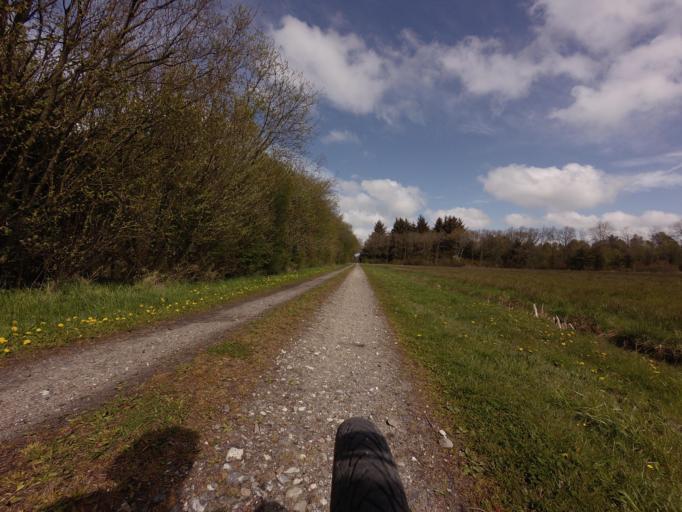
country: DK
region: North Denmark
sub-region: Jammerbugt Kommune
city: Kas
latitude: 57.1927
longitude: 9.5935
